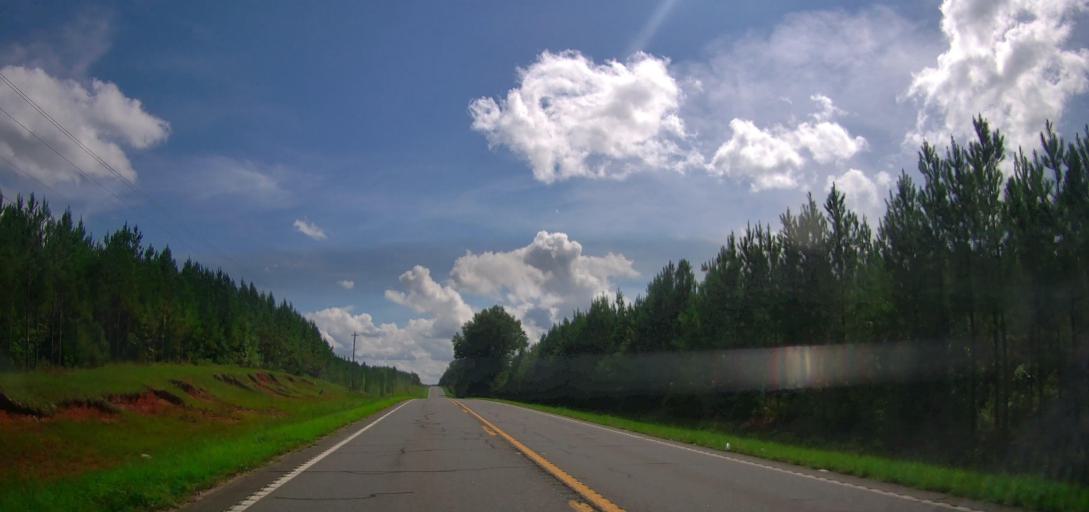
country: US
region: Georgia
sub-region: Talbot County
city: Talbotton
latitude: 32.7283
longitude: -84.5552
